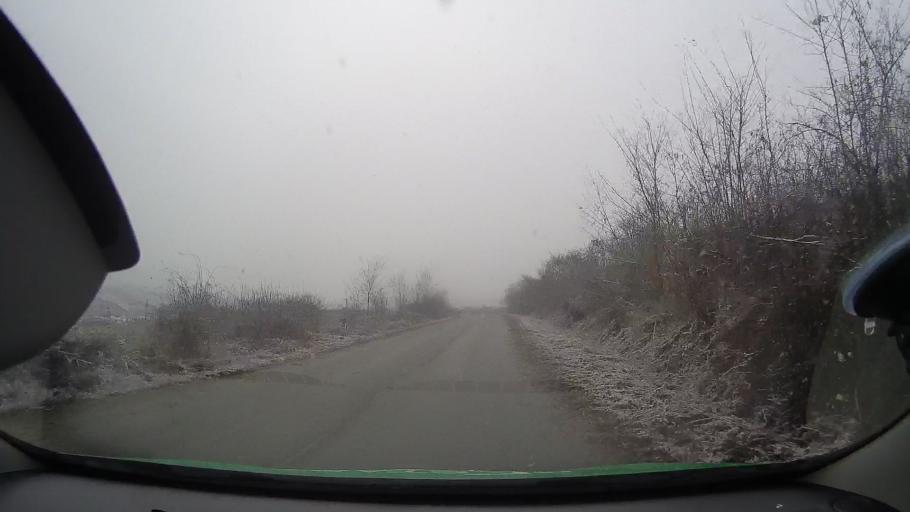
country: RO
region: Alba
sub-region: Comuna Noslac
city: Noslac
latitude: 46.3723
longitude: 23.9200
